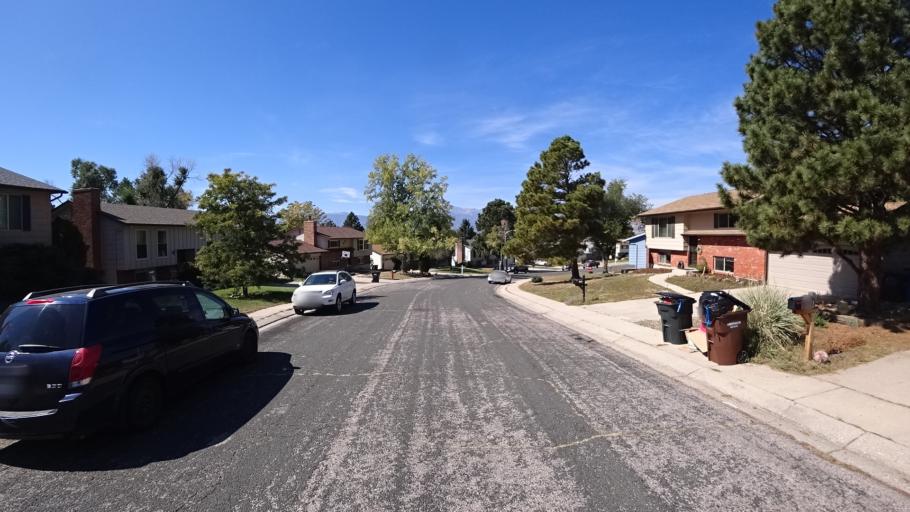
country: US
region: Colorado
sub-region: El Paso County
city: Cimarron Hills
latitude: 38.9138
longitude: -104.7662
